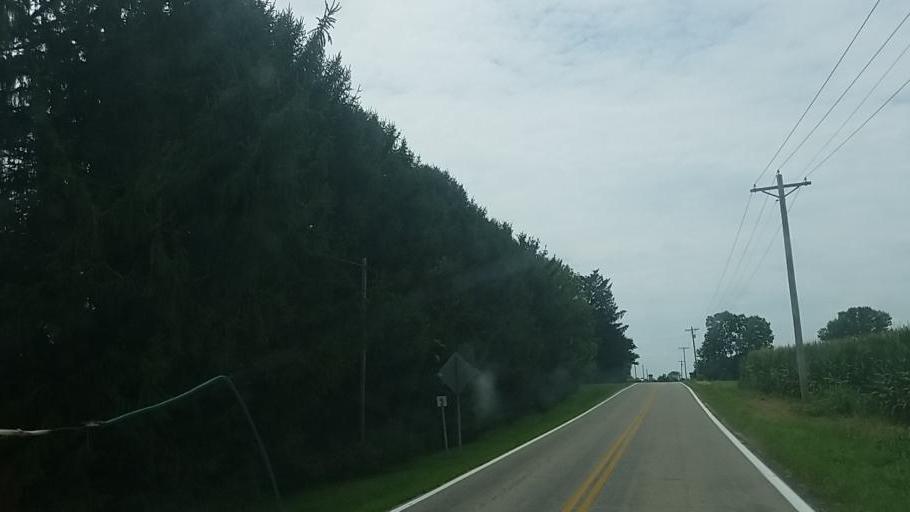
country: US
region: Ohio
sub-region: Pickaway County
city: Ashville
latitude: 39.7221
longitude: -82.8936
